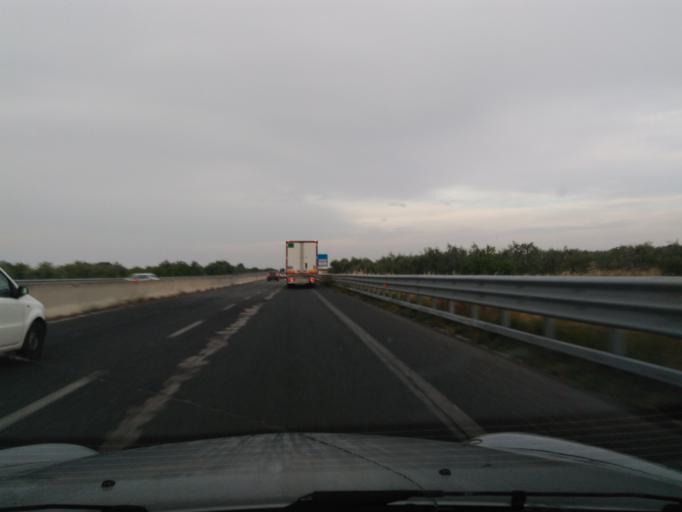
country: IT
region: Apulia
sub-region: Provincia di Bari
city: Molfetta
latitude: 41.1861
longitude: 16.6293
